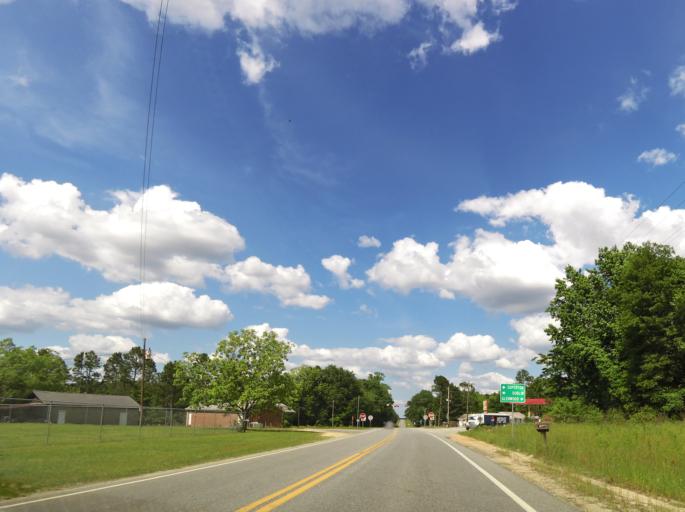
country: US
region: Georgia
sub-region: Wheeler County
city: Alamo
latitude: 32.2741
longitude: -82.7138
